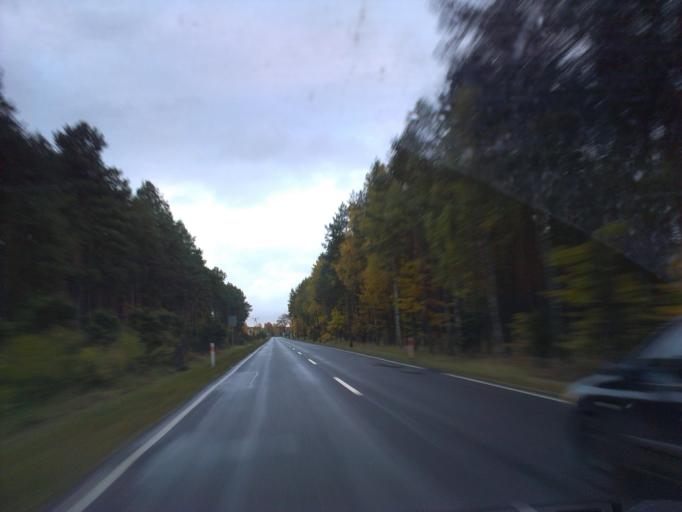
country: PL
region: Kujawsko-Pomorskie
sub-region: Powiat tucholski
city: Cekcyn
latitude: 53.5398
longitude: 17.9371
